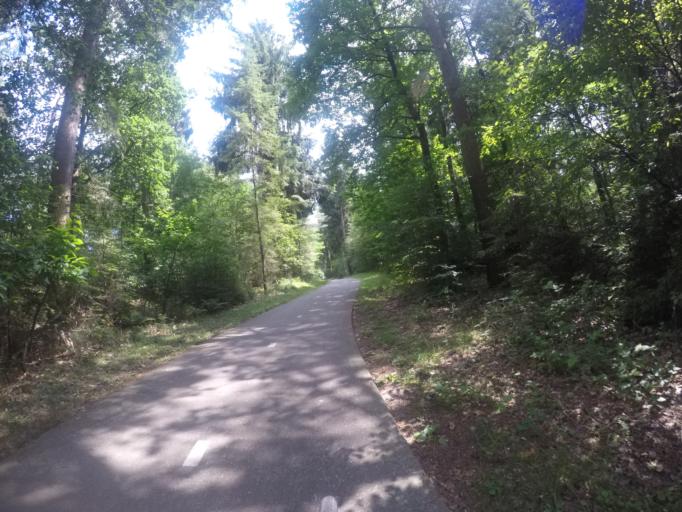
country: NL
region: Drenthe
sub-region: Gemeente Westerveld
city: Dwingeloo
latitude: 52.8866
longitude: 6.3191
